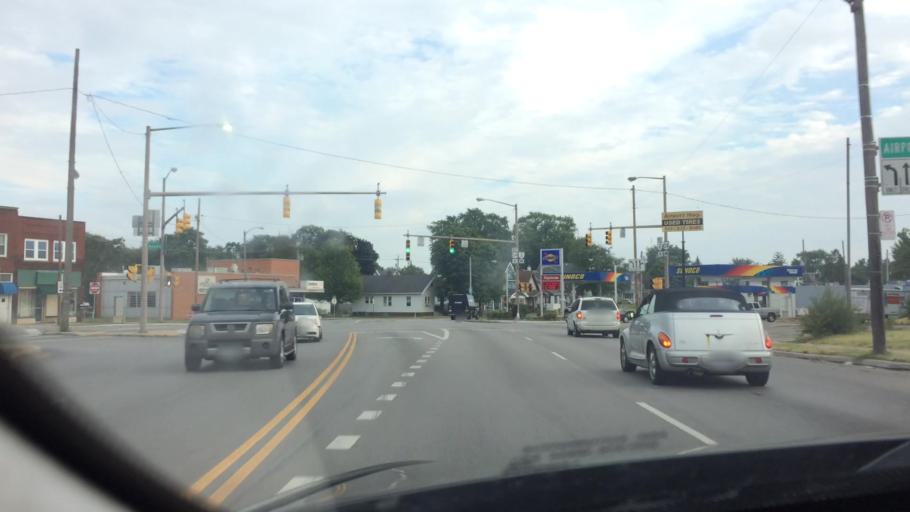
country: US
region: Ohio
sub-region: Wood County
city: Rossford
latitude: 41.6338
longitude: -83.5907
